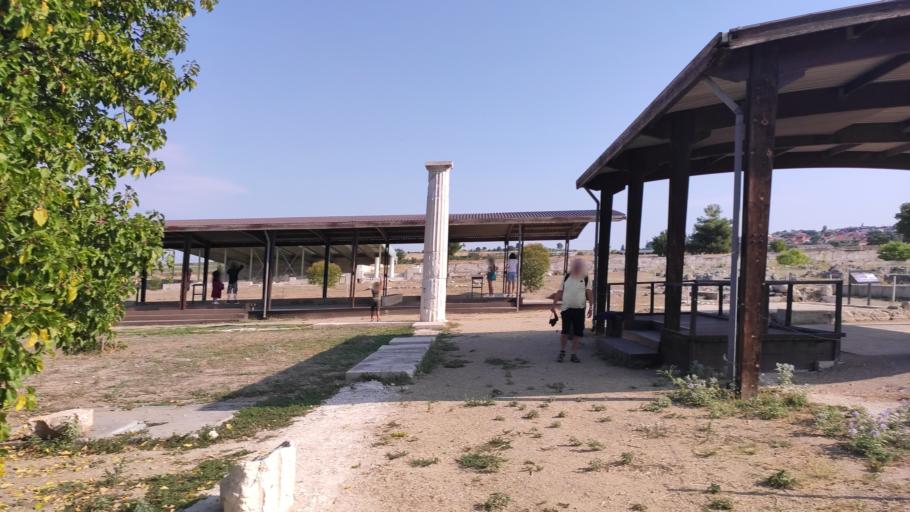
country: GR
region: Central Macedonia
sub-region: Nomos Pellis
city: Pella
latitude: 40.7543
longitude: 22.5178
